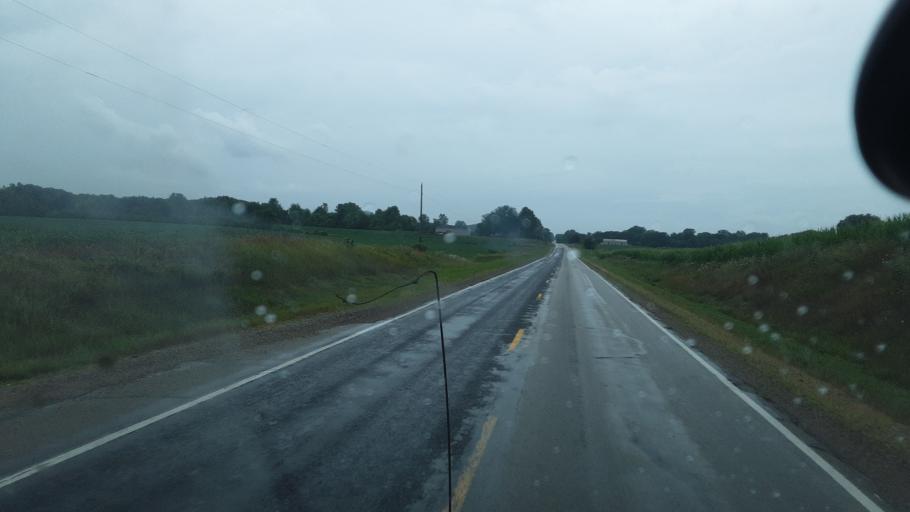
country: US
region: Indiana
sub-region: Steuben County
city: Hamilton
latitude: 41.5591
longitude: -84.8222
